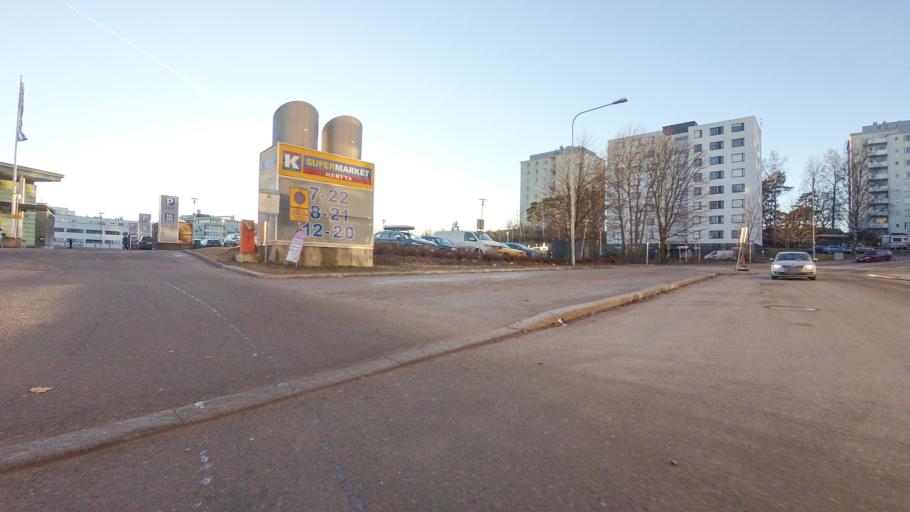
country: FI
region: Uusimaa
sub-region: Helsinki
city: Helsinki
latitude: 60.1947
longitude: 25.0283
